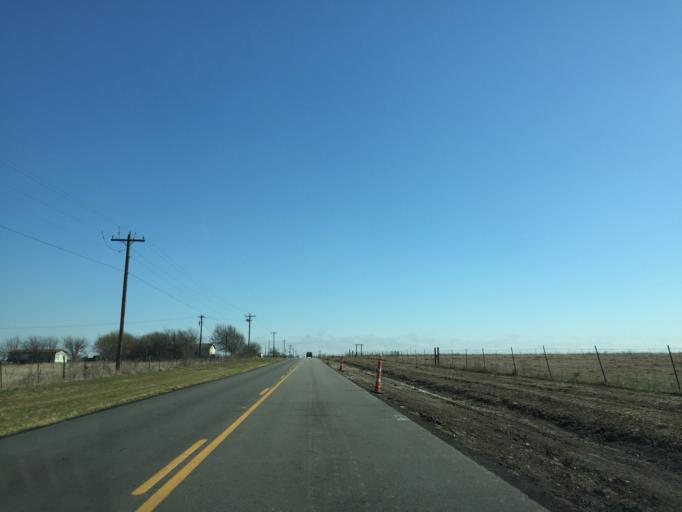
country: US
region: Texas
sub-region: Williamson County
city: Serenada
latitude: 30.7272
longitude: -97.6309
